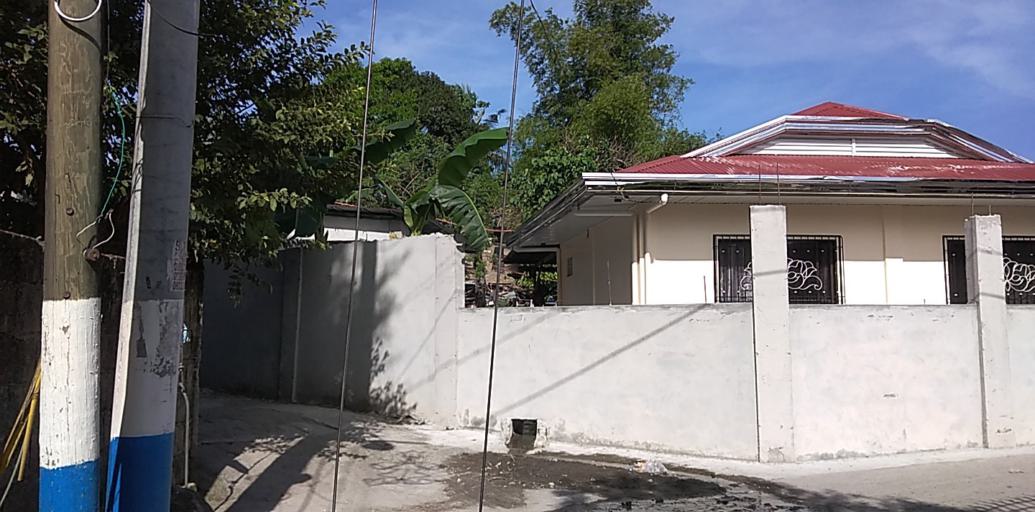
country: PH
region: Central Luzon
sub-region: Province of Pampanga
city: Porac
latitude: 15.0773
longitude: 120.5392
